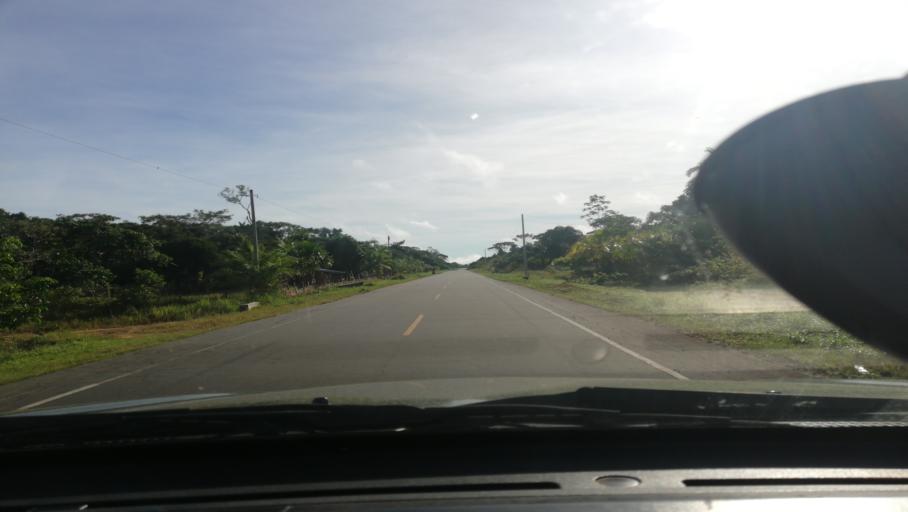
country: PE
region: Loreto
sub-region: Provincia de Loreto
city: Nauta
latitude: -4.3630
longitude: -73.5575
